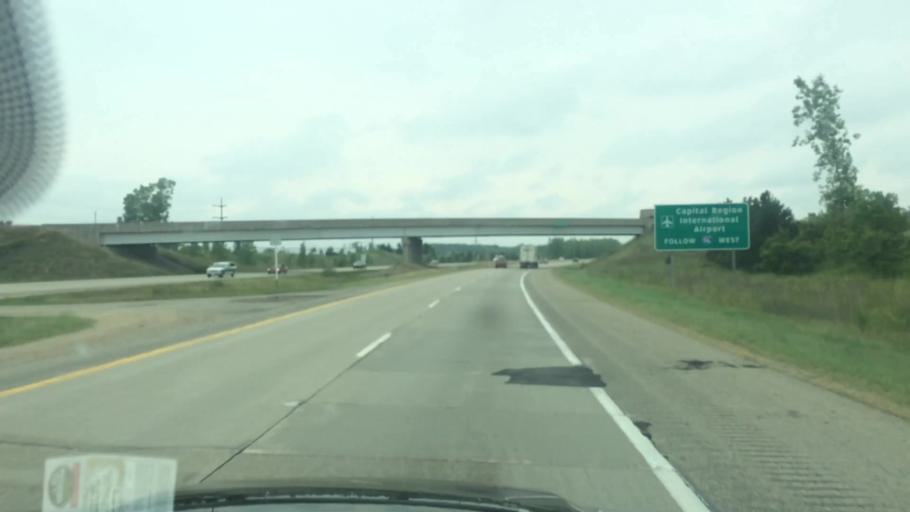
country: US
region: Michigan
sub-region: Eaton County
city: Dimondale
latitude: 42.6817
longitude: -84.6795
